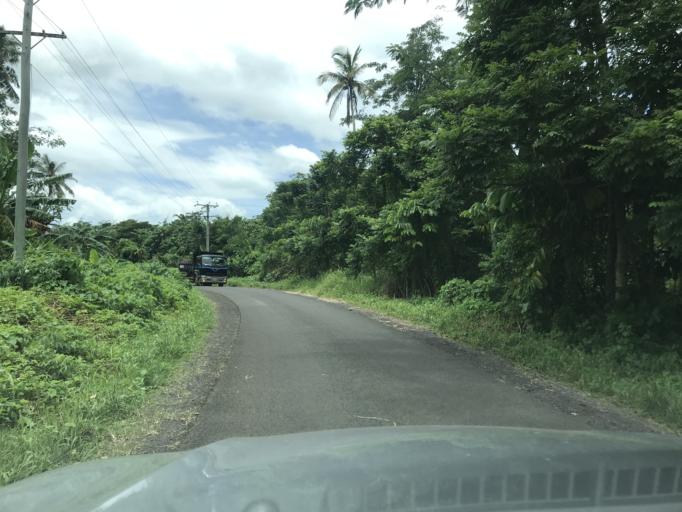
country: WS
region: Tuamasaga
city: Afenga
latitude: -13.8150
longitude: -171.8858
